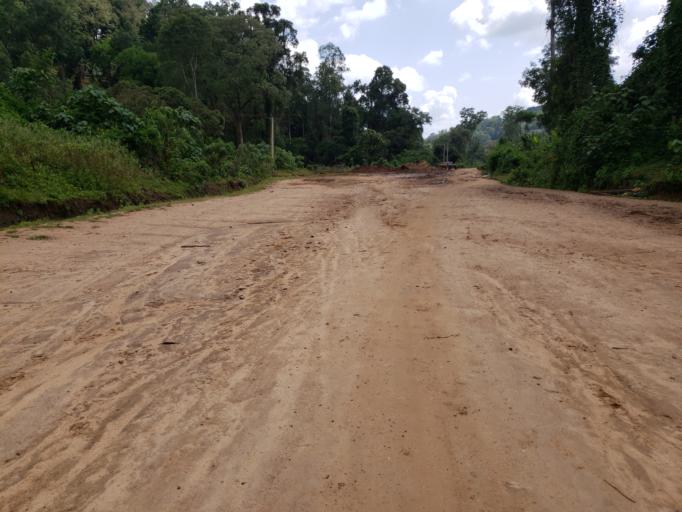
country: ET
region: Oromiya
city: Dodola
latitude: 6.4580
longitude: 39.5701
